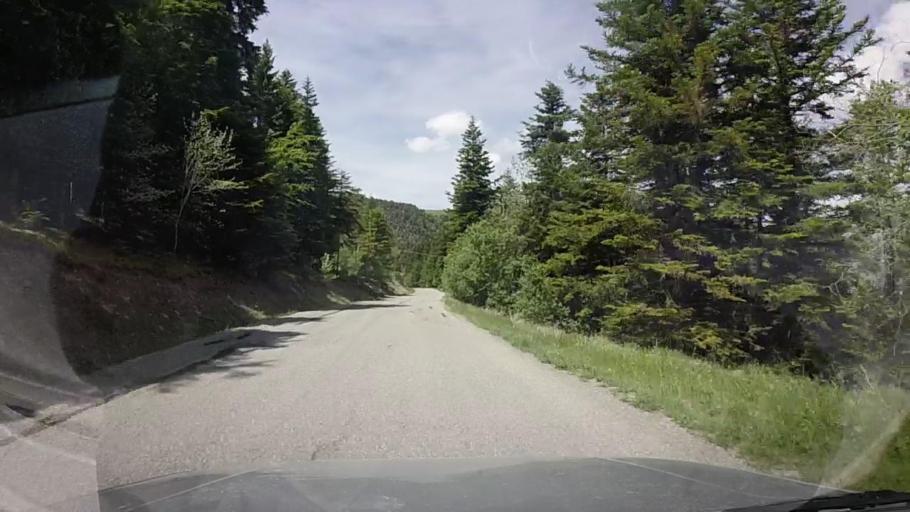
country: FR
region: Provence-Alpes-Cote d'Azur
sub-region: Departement des Alpes-de-Haute-Provence
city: Seyne-les-Alpes
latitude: 44.3536
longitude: 6.2968
